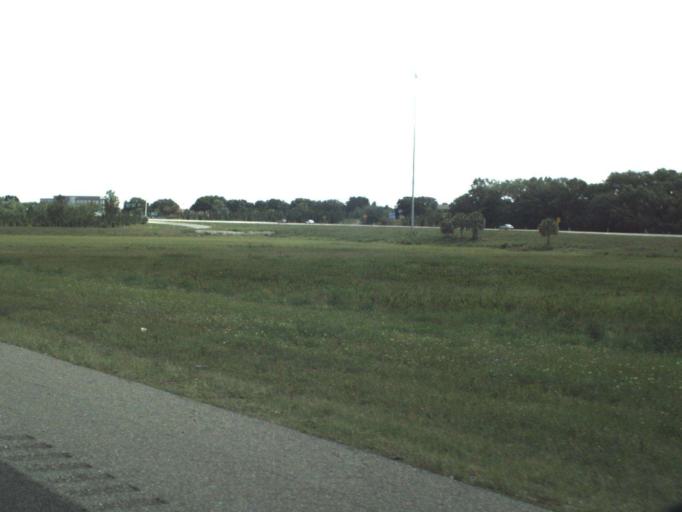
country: US
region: Florida
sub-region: Seminole County
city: Heathrow
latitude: 28.7523
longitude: -81.3645
